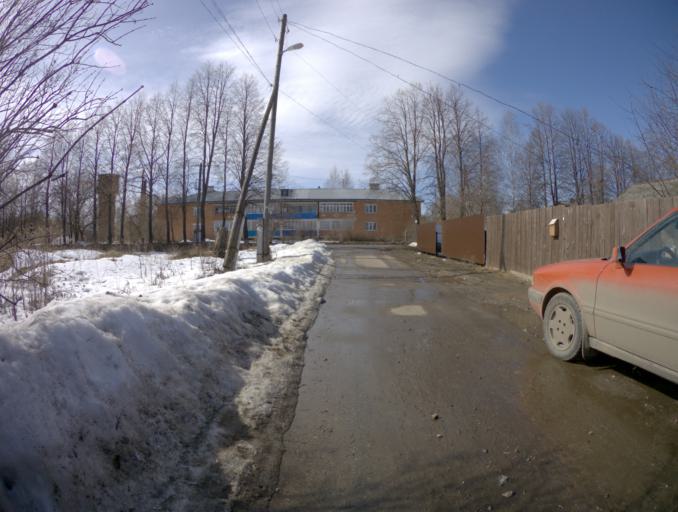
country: RU
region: Vladimir
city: Suzdal'
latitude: 56.4240
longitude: 40.4284
